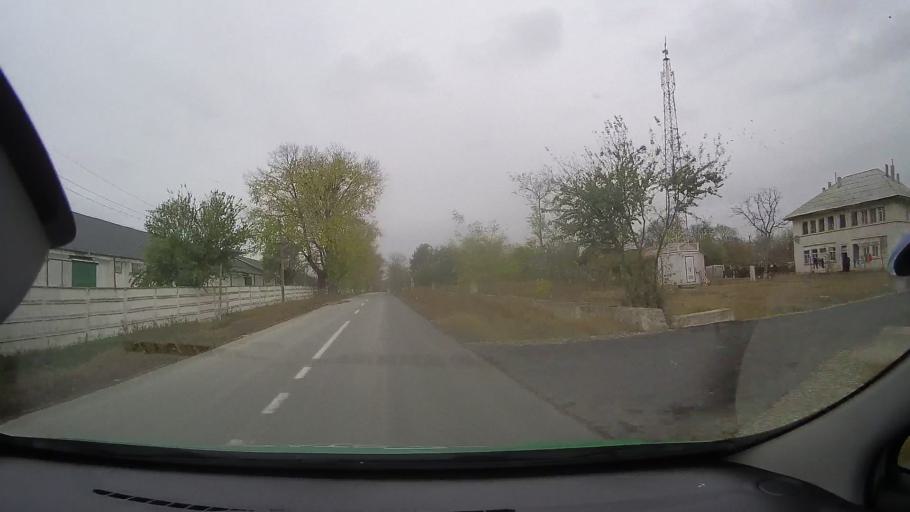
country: RO
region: Constanta
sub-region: Comuna Pantelimon
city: Pantelimon
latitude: 44.5490
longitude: 28.3296
